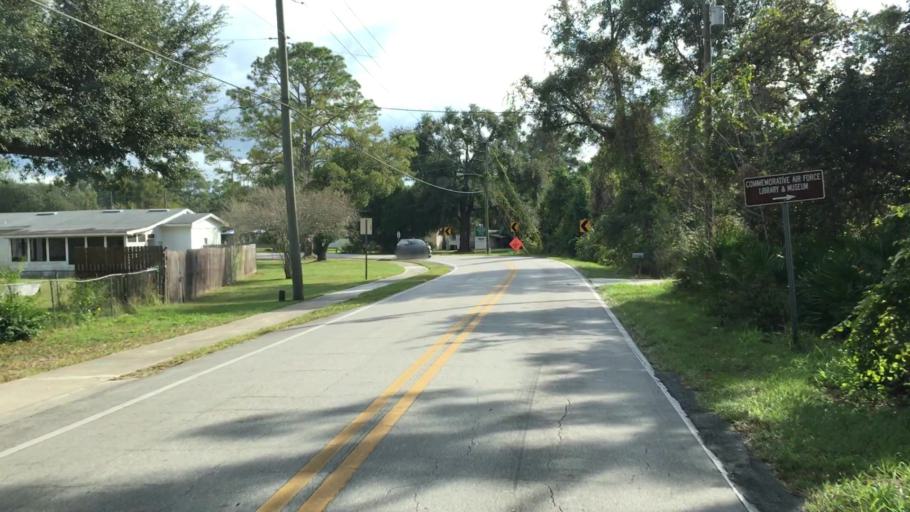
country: US
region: Florida
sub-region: Volusia County
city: North DeLand
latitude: 29.0669
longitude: -81.2713
